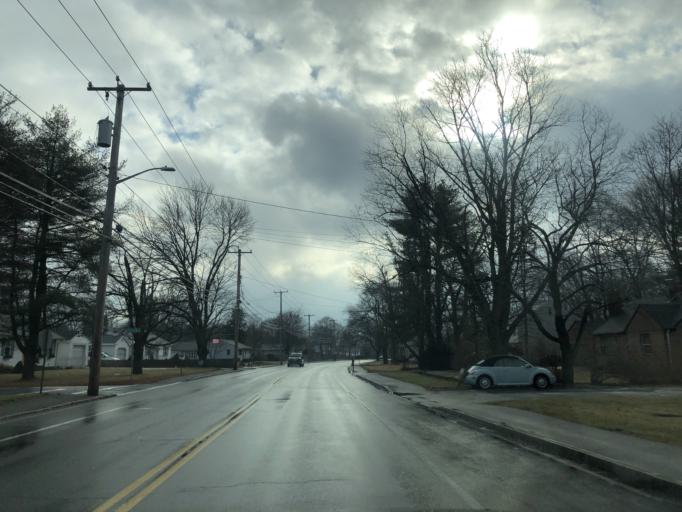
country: US
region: Massachusetts
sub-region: Norfolk County
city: Plainville
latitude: 42.0051
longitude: -71.2991
